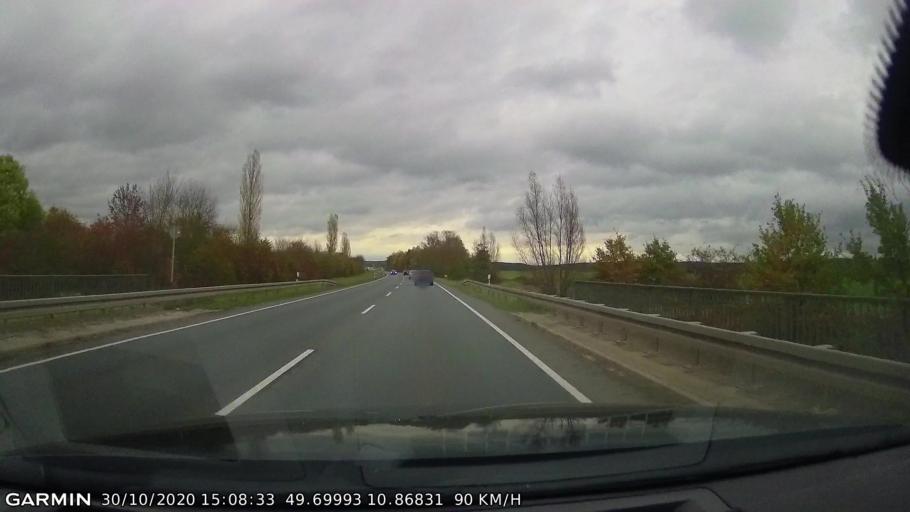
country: DE
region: Bavaria
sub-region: Regierungsbezirk Mittelfranken
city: Adelsdorf
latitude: 49.6995
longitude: 10.8679
